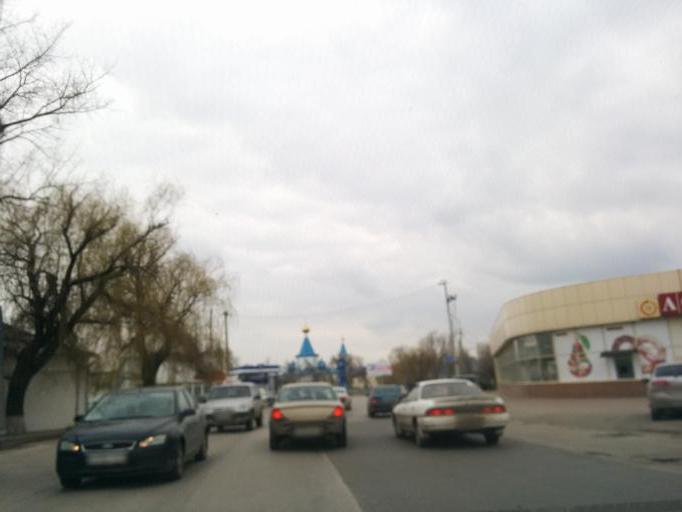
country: RU
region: Rostov
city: Novocherkassk
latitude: 47.4465
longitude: 40.1043
